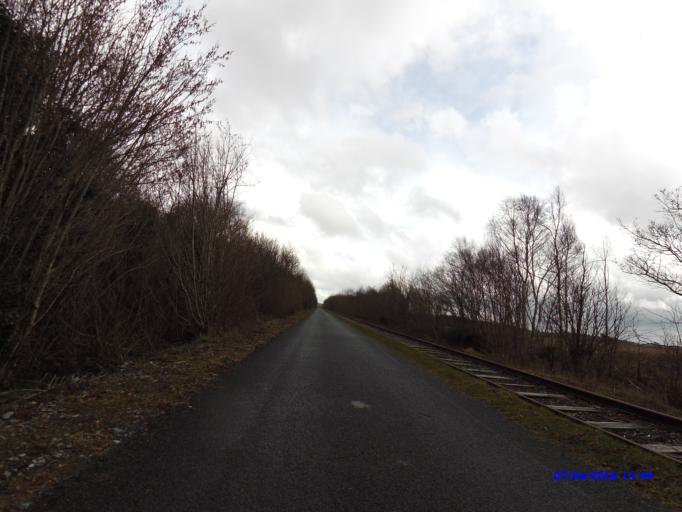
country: IE
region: Leinster
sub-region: An Iarmhi
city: Athlone
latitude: 53.4161
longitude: -7.8645
